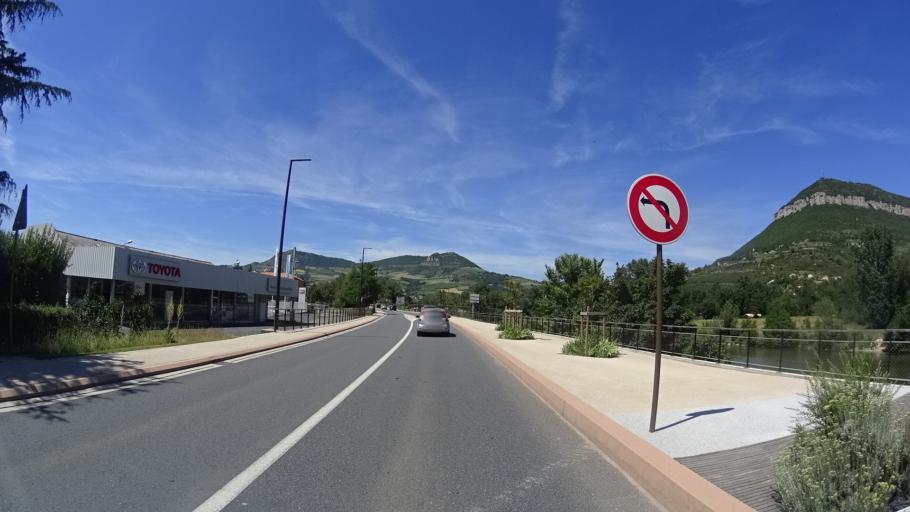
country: FR
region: Midi-Pyrenees
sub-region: Departement de l'Aveyron
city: Millau
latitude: 44.0989
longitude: 3.0874
